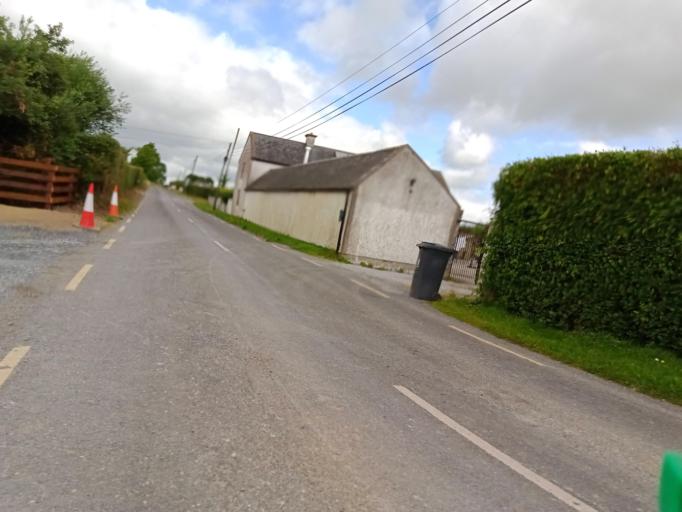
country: IE
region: Leinster
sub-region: Kilkenny
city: Callan
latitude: 52.5546
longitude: -7.4093
